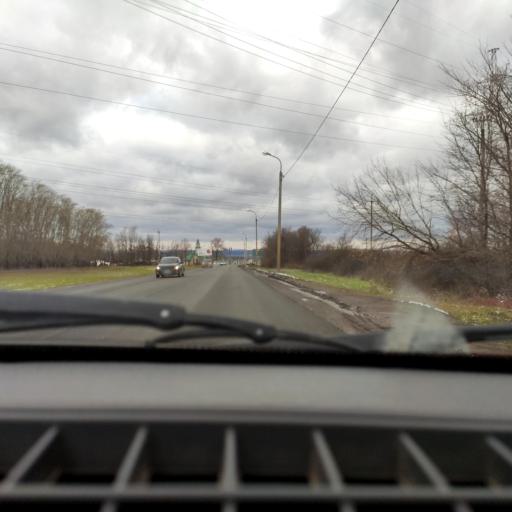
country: RU
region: Bashkortostan
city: Kabakovo
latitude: 54.6318
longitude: 56.0976
